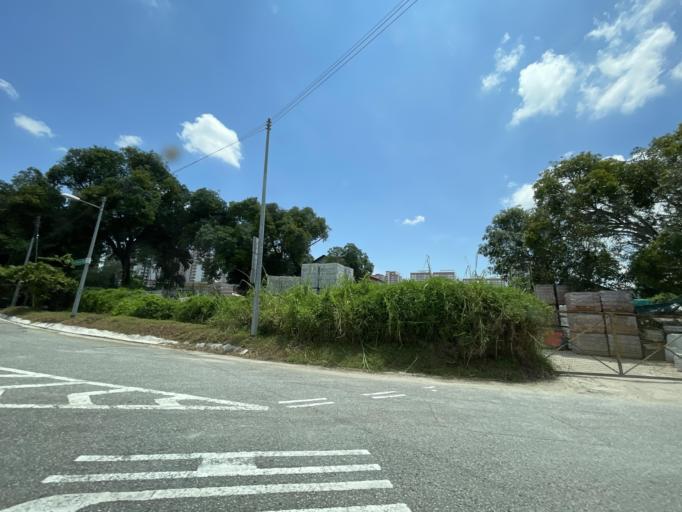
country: MY
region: Johor
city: Kampung Pasir Gudang Baru
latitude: 1.3833
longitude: 103.8775
